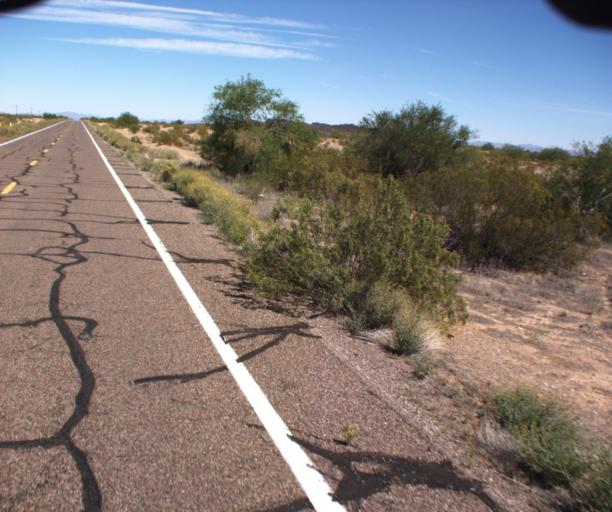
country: US
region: Arizona
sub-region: Maricopa County
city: Gila Bend
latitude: 32.7941
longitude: -112.8028
